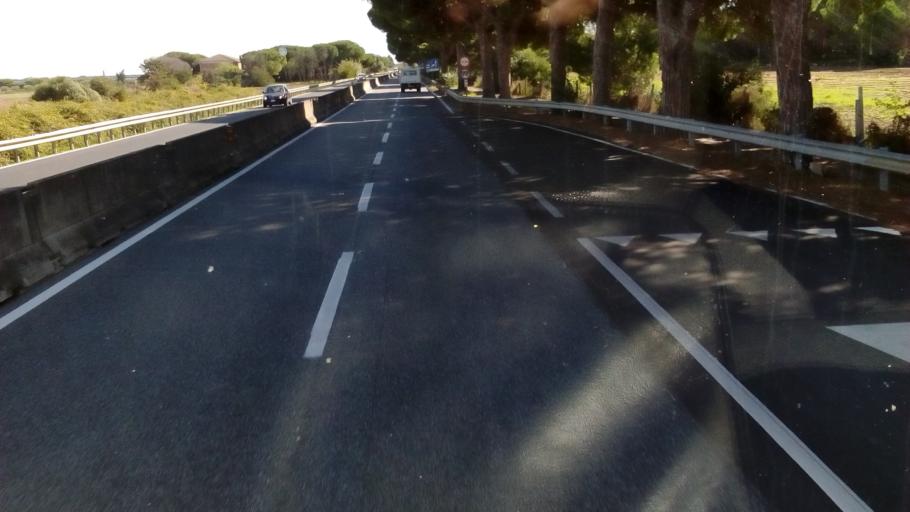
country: IT
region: Tuscany
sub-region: Provincia di Grosseto
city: Albinia
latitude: 42.5187
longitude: 11.1931
